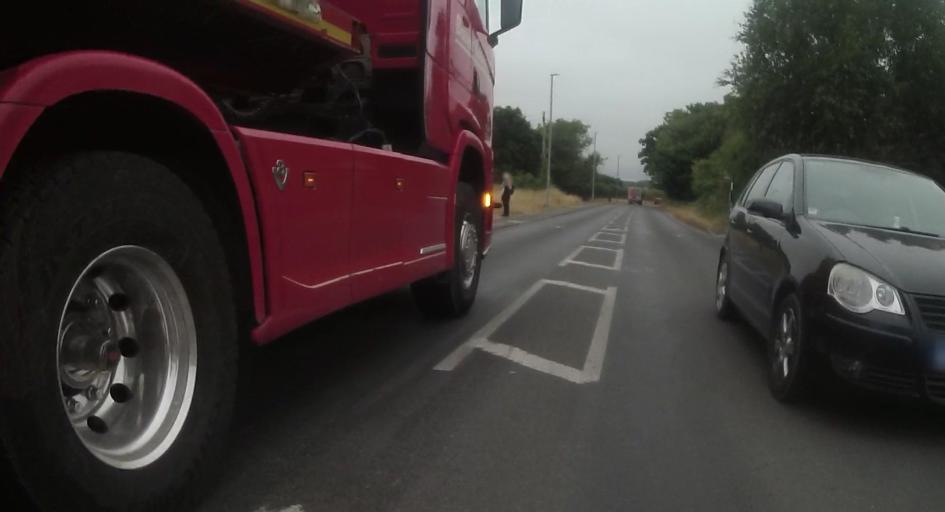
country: GB
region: England
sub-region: Dorset
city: Wareham
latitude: 50.6724
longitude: -2.1070
